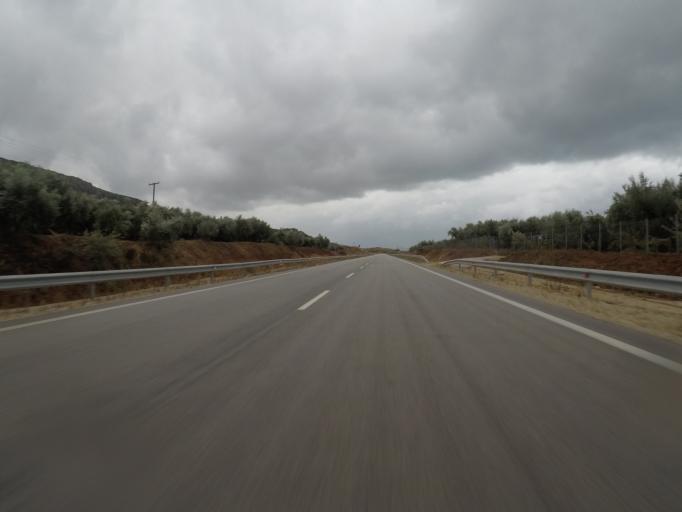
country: GR
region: Peloponnese
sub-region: Nomos Messinias
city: Gargalianoi
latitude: 37.0273
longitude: 21.6331
